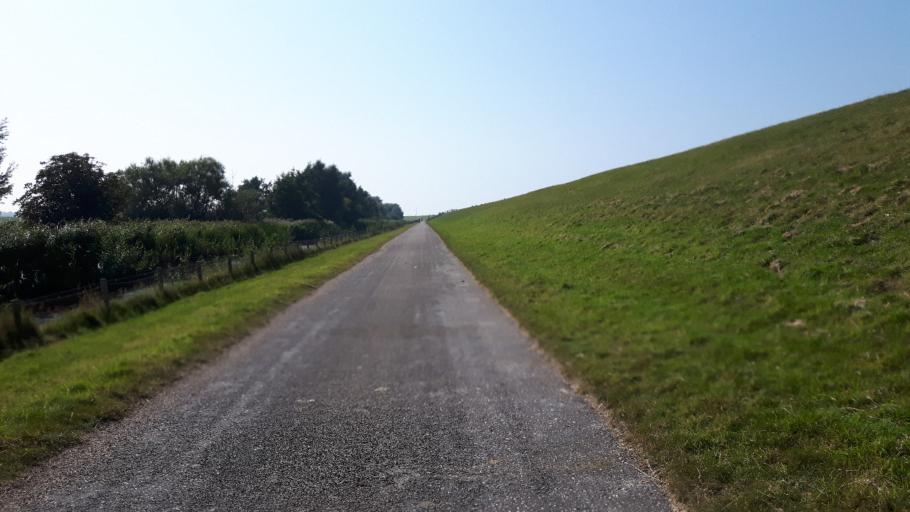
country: NL
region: Friesland
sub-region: Sudwest Fryslan
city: Workum
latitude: 52.9662
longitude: 5.4231
